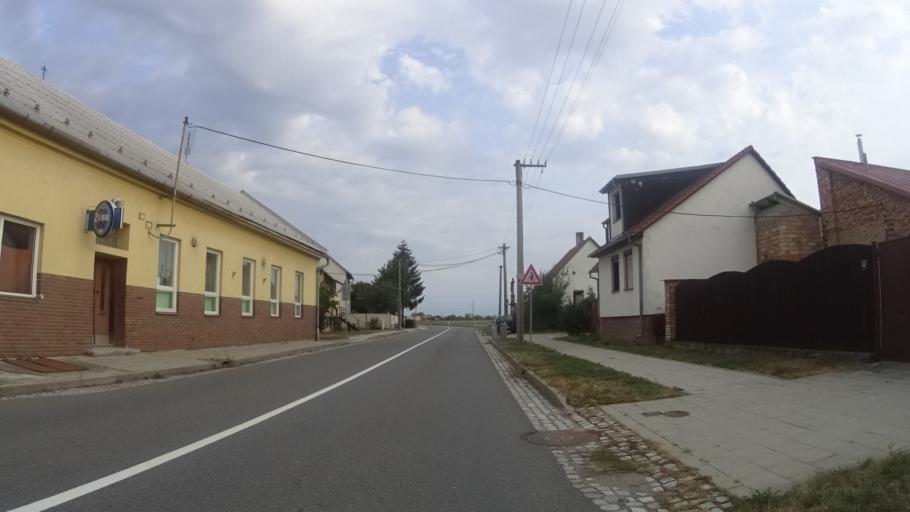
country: CZ
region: Zlin
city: Chropyne
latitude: 49.3413
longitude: 17.3806
